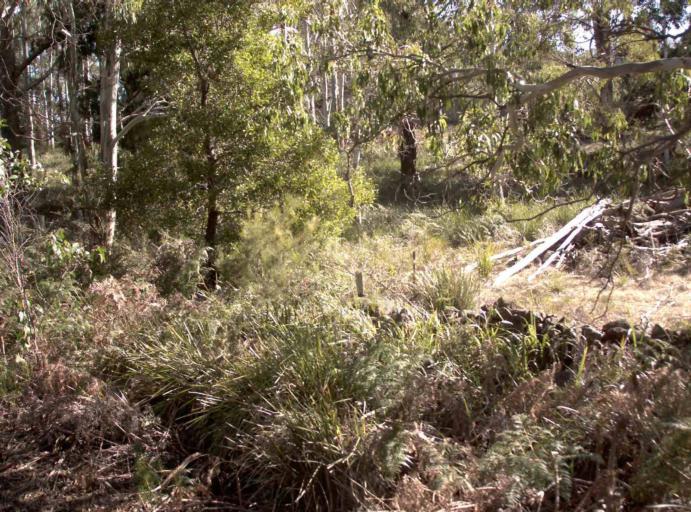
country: AU
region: Tasmania
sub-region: Launceston
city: Mayfield
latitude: -41.3113
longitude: 147.2037
